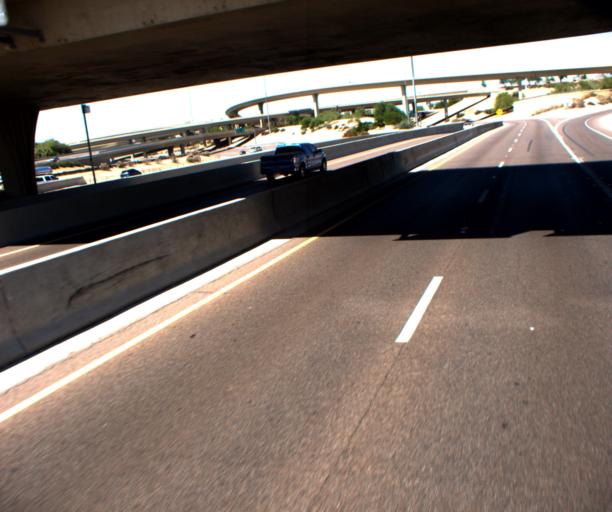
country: US
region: Arizona
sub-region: Maricopa County
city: Phoenix
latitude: 33.4585
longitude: -112.0366
